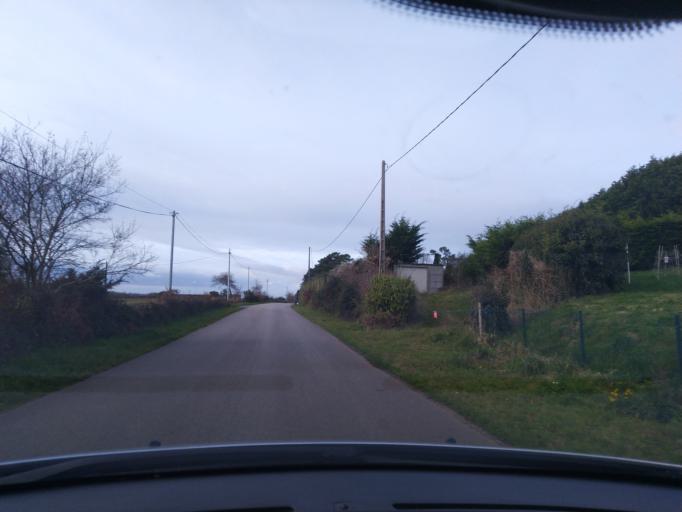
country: FR
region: Brittany
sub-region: Departement du Finistere
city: Guerlesquin
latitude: 48.5282
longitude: -3.6058
